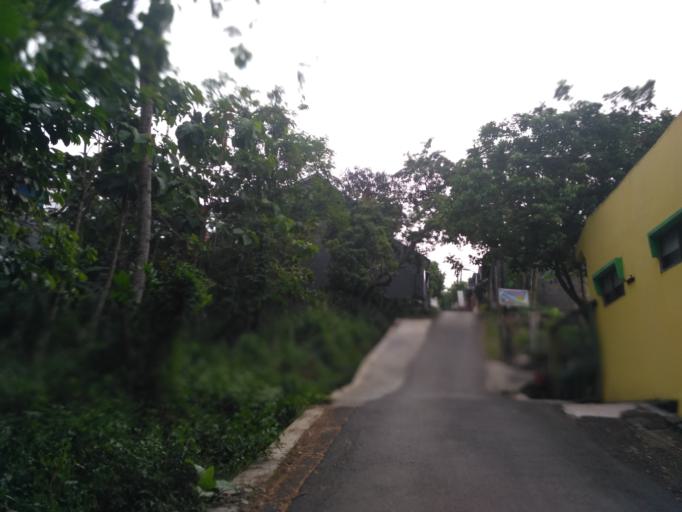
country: ID
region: Central Java
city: Ungaran
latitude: -7.0751
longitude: 110.4237
